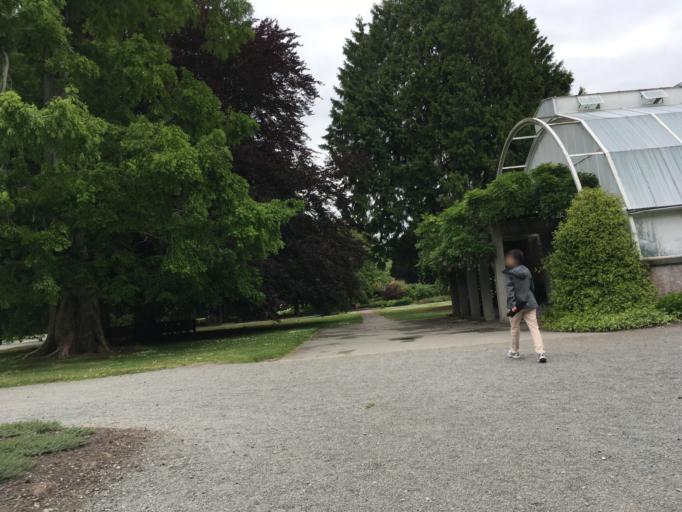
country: NZ
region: Canterbury
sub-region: Christchurch City
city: Christchurch
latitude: -43.5295
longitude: 172.6214
